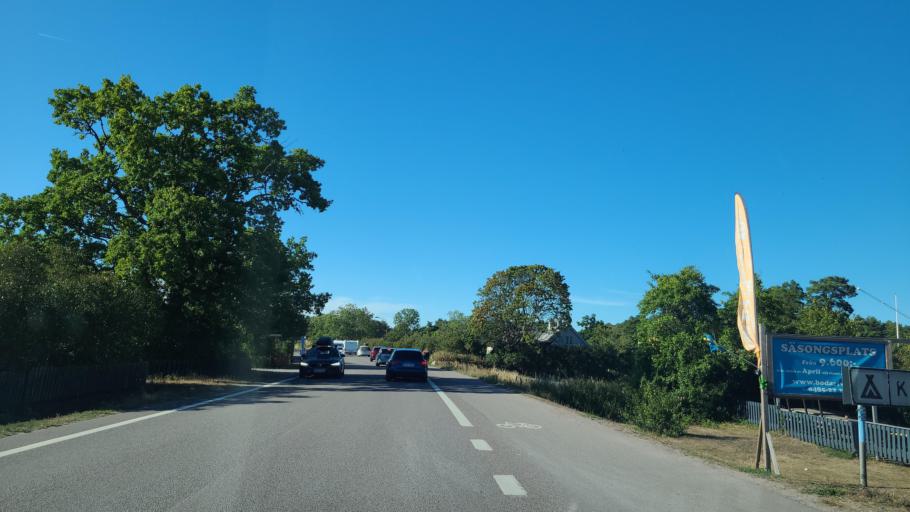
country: SE
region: Kalmar
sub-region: Borgholms Kommun
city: Borgholm
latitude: 57.2489
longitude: 17.0576
